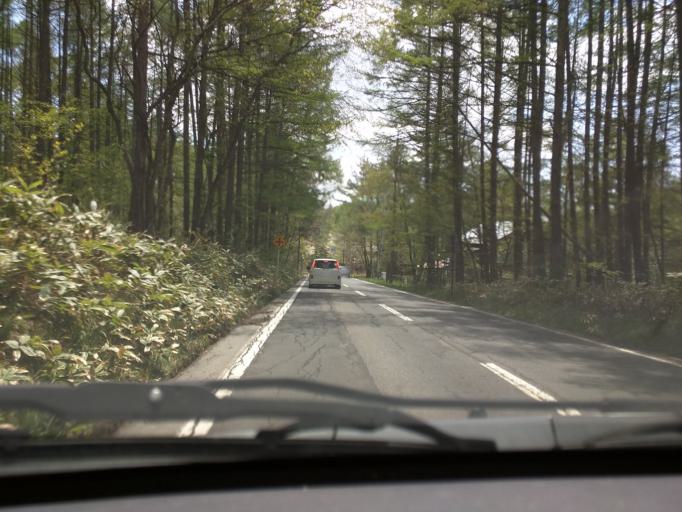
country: JP
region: Nagano
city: Nagano-shi
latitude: 36.7058
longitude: 138.1334
